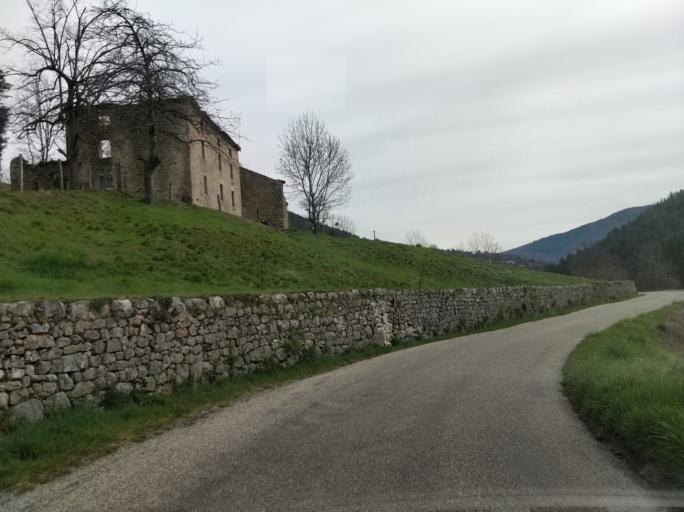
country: FR
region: Rhone-Alpes
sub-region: Departement de l'Ardeche
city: Satillieu
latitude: 45.1595
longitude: 4.5865
